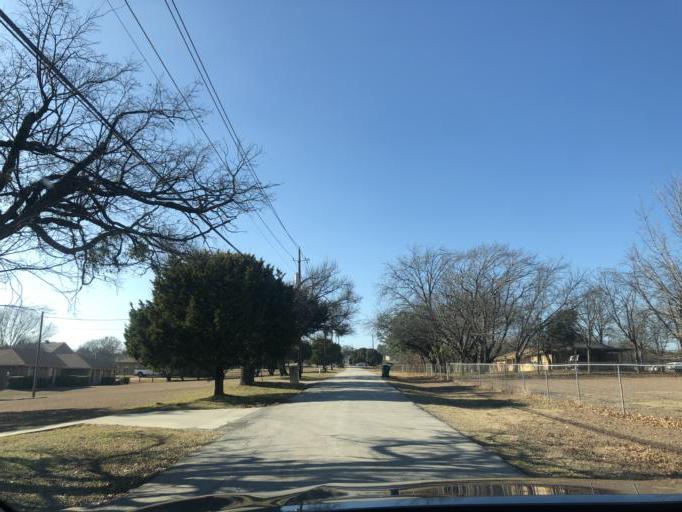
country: US
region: Texas
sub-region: Dallas County
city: Cedar Hill
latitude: 32.6119
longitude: -96.9364
